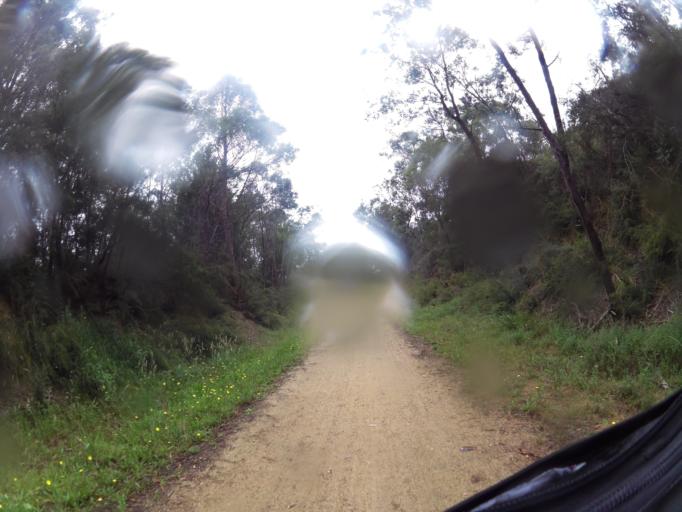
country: AU
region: Victoria
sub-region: East Gippsland
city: Bairnsdale
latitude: -37.7460
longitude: 147.8104
